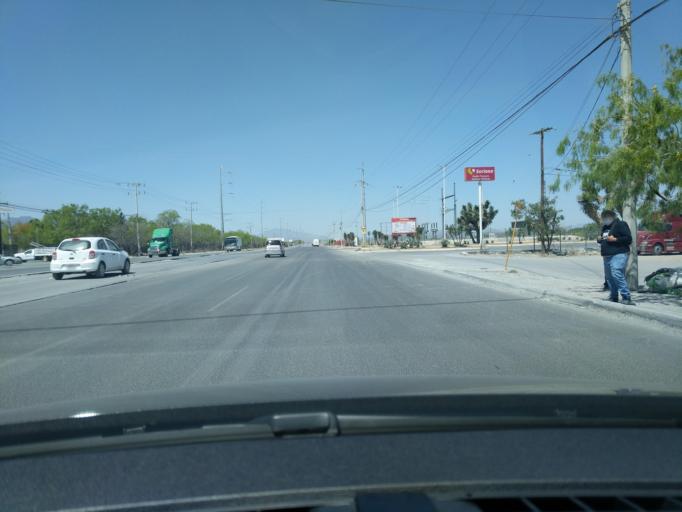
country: MX
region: Nuevo Leon
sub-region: Salinas Victoria
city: Emiliano Zapata
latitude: 25.8922
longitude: -100.2592
